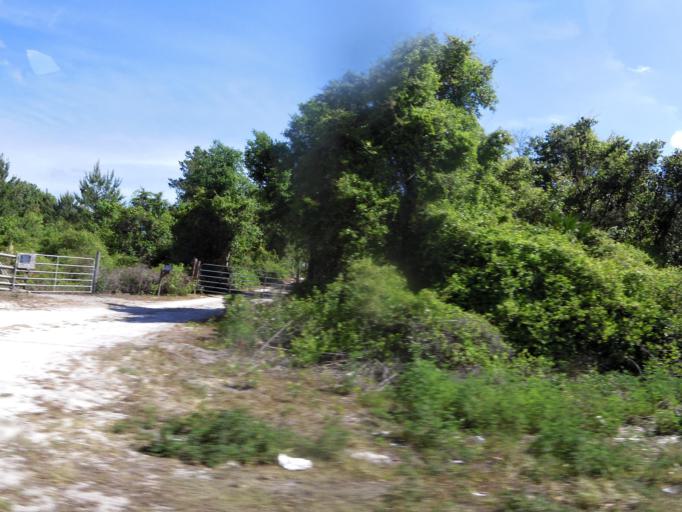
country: US
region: Florida
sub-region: Volusia County
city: Lake Helen
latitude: 28.9325
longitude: -81.2014
